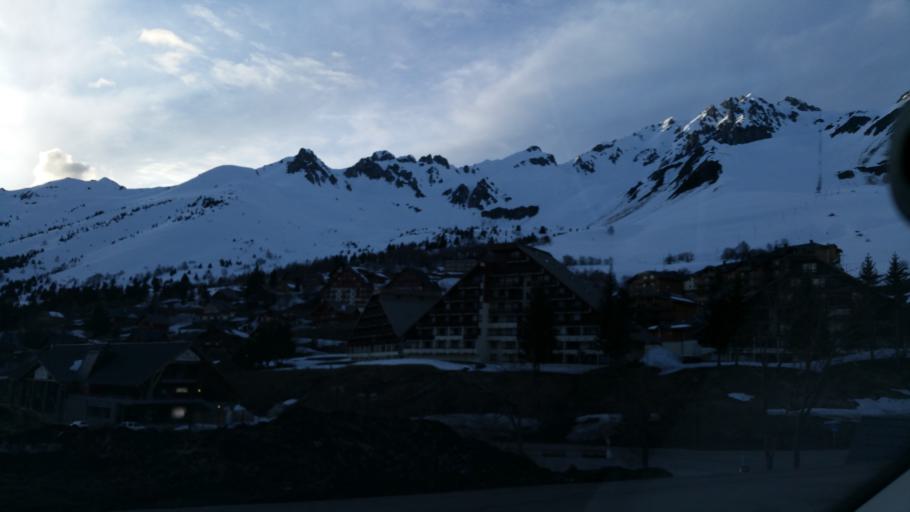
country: FR
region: Rhone-Alpes
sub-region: Departement de la Savoie
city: La Chambre
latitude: 45.4195
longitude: 6.3647
